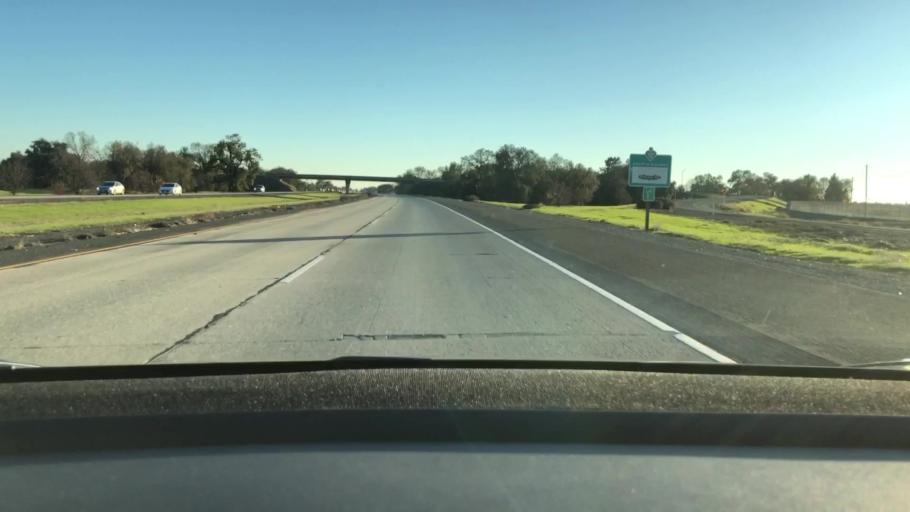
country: US
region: California
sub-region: Yolo County
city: Woodland
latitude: 38.6225
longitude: -121.7668
